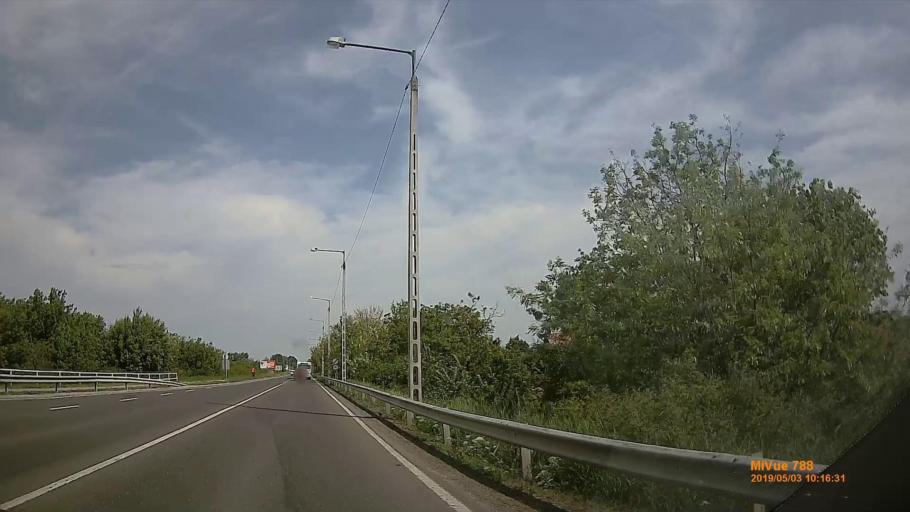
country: HU
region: Jasz-Nagykun-Szolnok
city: Szolnok
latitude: 47.1572
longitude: 20.2034
